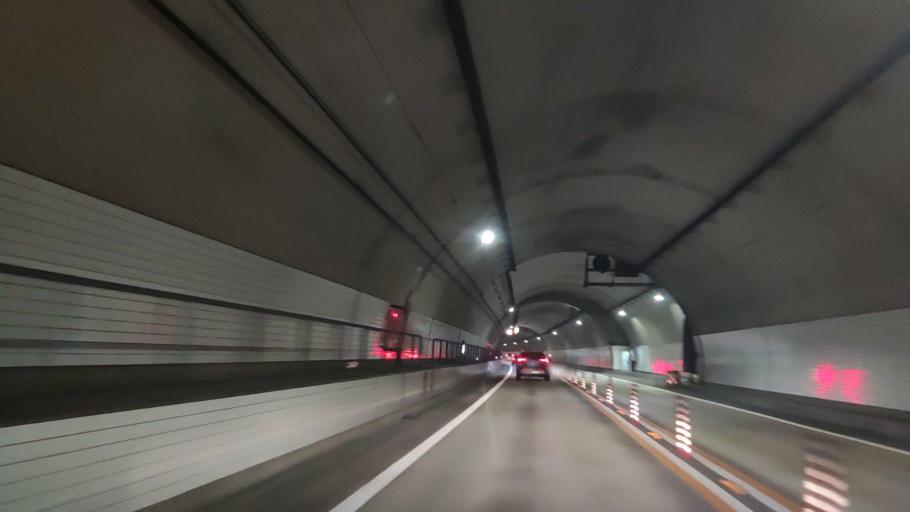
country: JP
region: Kyoto
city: Miyazu
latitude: 35.5617
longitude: 135.1221
